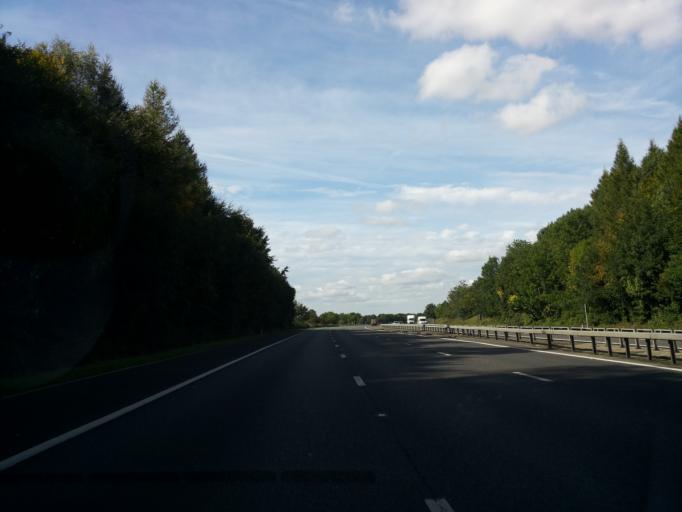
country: GB
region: England
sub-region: Kent
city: Borough Green
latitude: 51.3190
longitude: 0.2845
